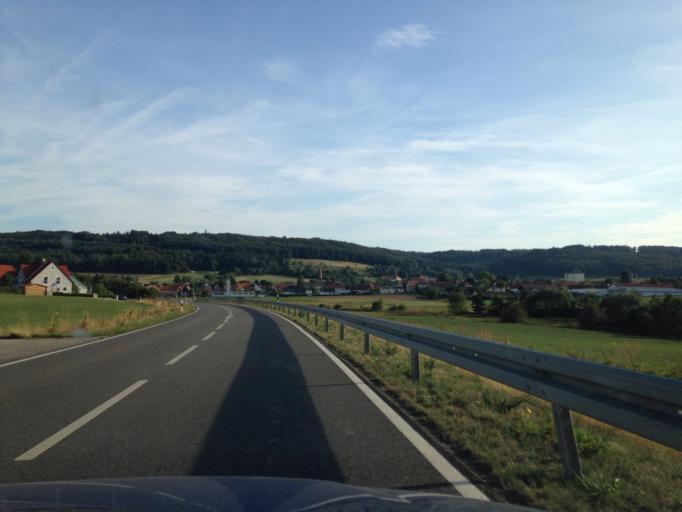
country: DE
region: Bavaria
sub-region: Regierungsbezirk Mittelfranken
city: Thalmassing
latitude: 49.0947
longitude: 11.2186
